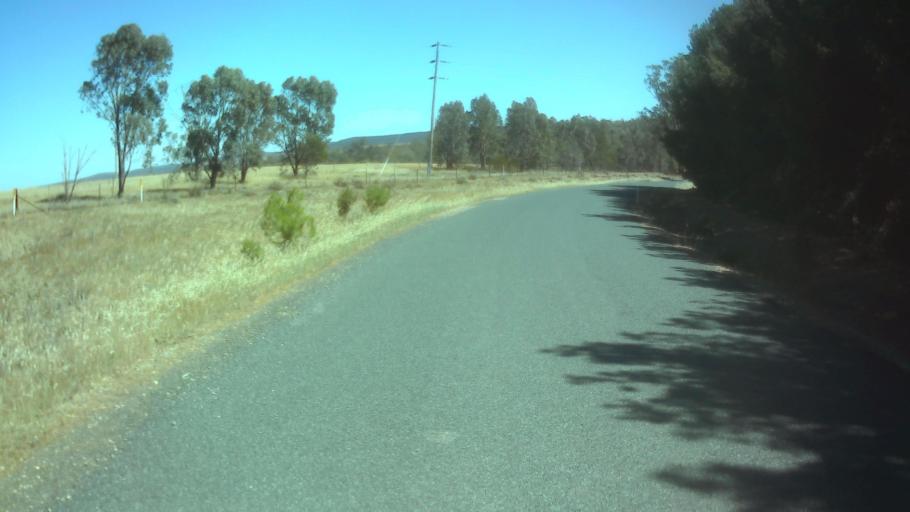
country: AU
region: New South Wales
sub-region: Weddin
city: Grenfell
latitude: -33.9410
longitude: 148.3852
